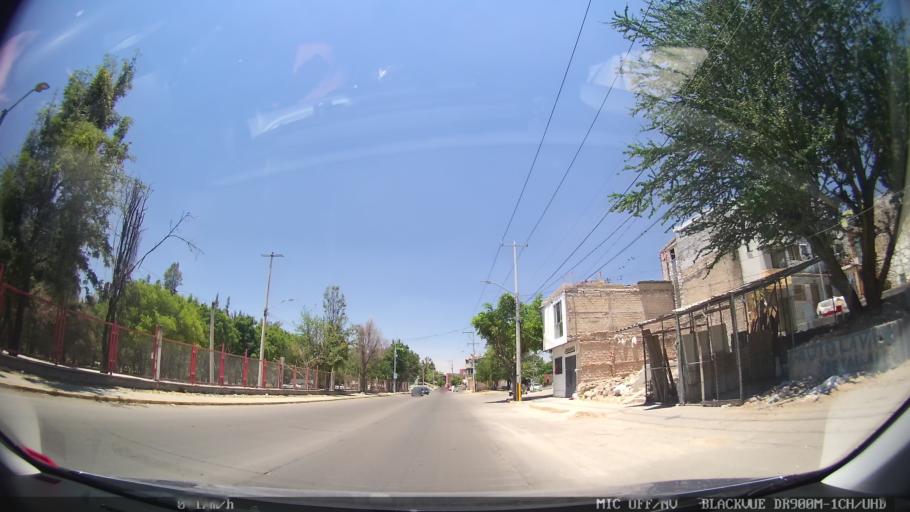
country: MX
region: Jalisco
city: Tlaquepaque
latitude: 20.6749
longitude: -103.2690
